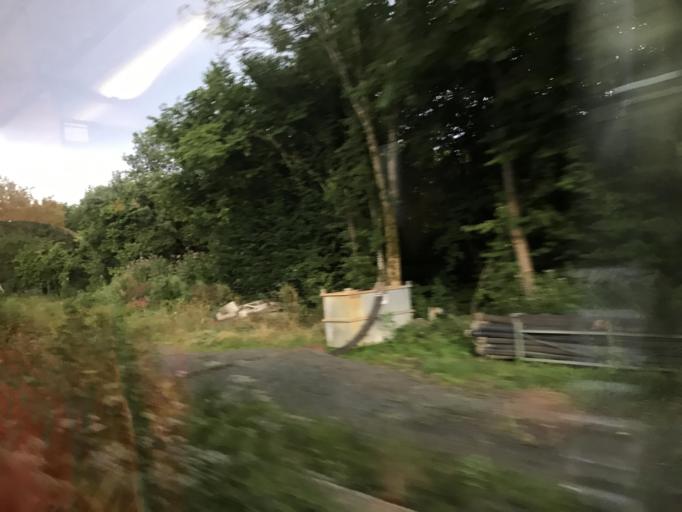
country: DE
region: Rheinland-Pfalz
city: Brachbach
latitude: 50.8209
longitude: 7.9379
